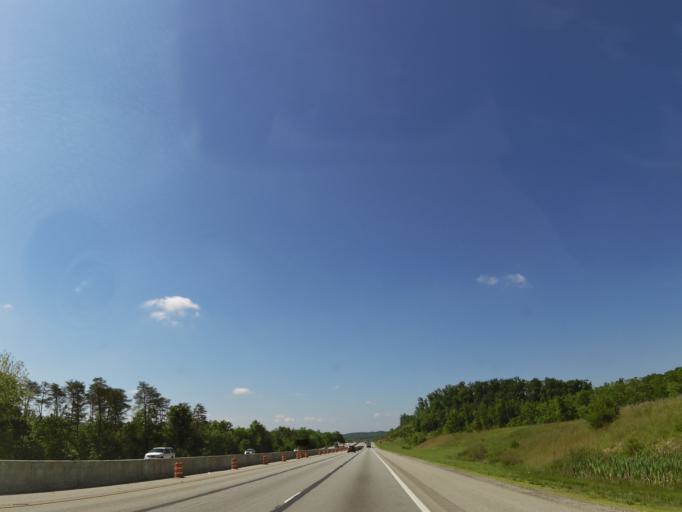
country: US
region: Kentucky
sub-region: Madison County
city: Berea
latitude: 37.4932
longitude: -84.3293
